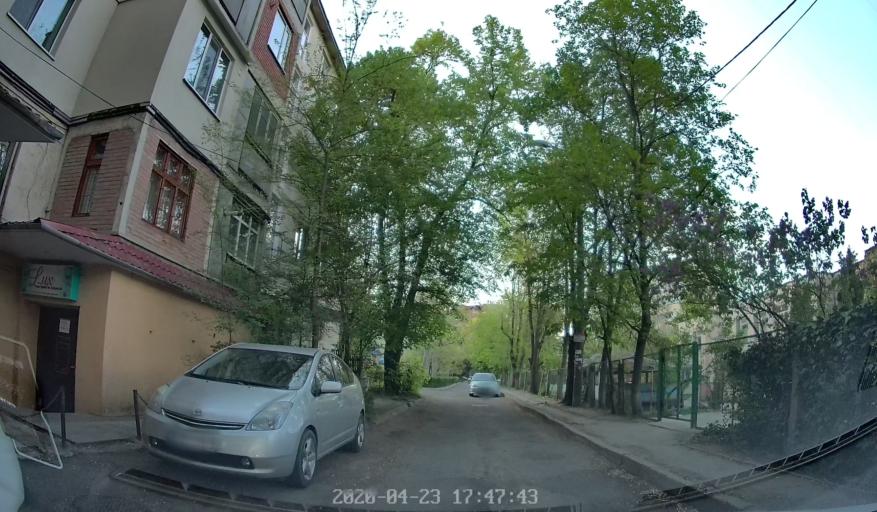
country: MD
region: Chisinau
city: Chisinau
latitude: 47.0004
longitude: 28.8192
